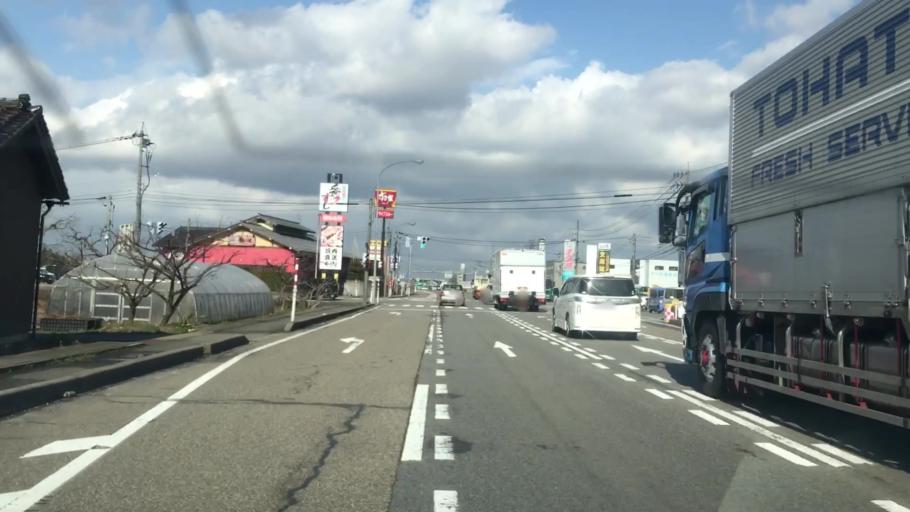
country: JP
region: Toyama
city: Kuragaki-kosugi
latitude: 36.7167
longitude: 137.0817
